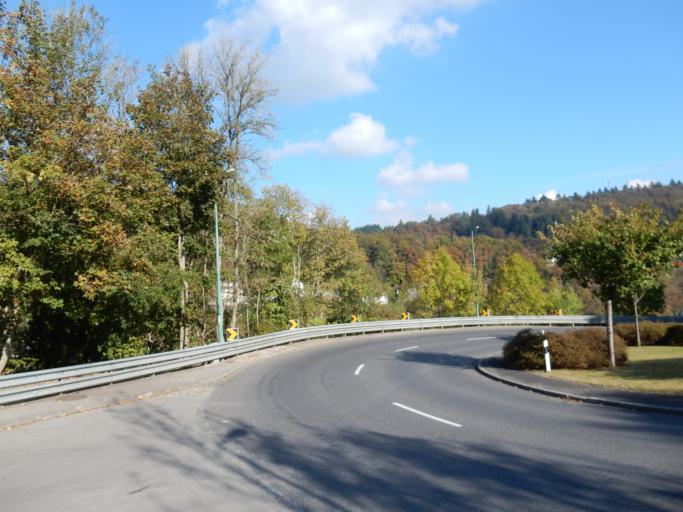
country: LU
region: Diekirch
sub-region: Canton de Clervaux
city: Clervaux
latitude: 50.0534
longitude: 6.0246
